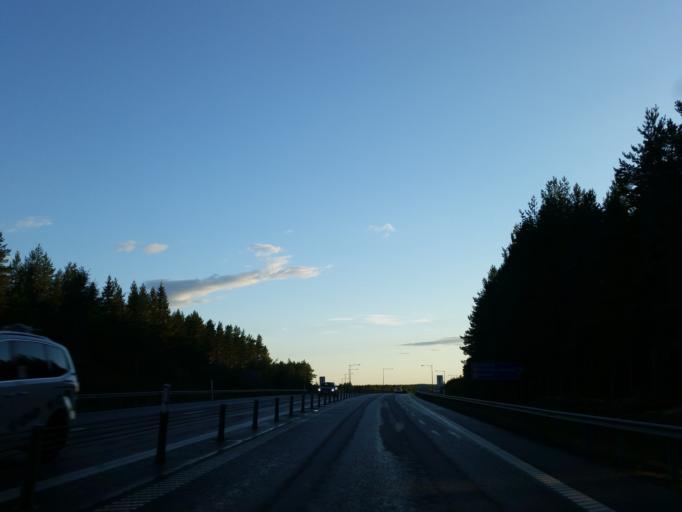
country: SE
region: Vaesterbotten
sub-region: Umea Kommun
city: Saevar
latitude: 63.9019
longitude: 20.5730
